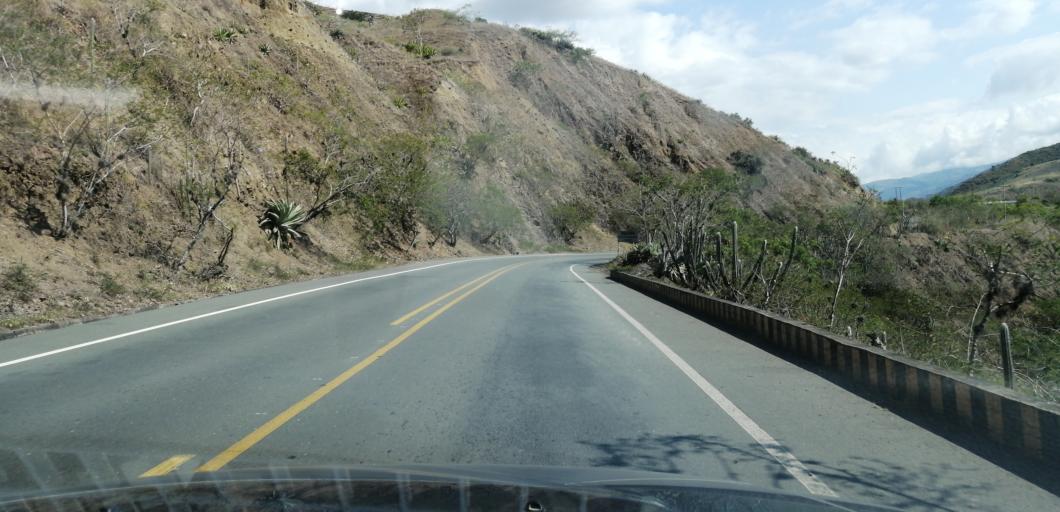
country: CO
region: Valle del Cauca
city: Dagua
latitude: 3.7498
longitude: -76.6615
